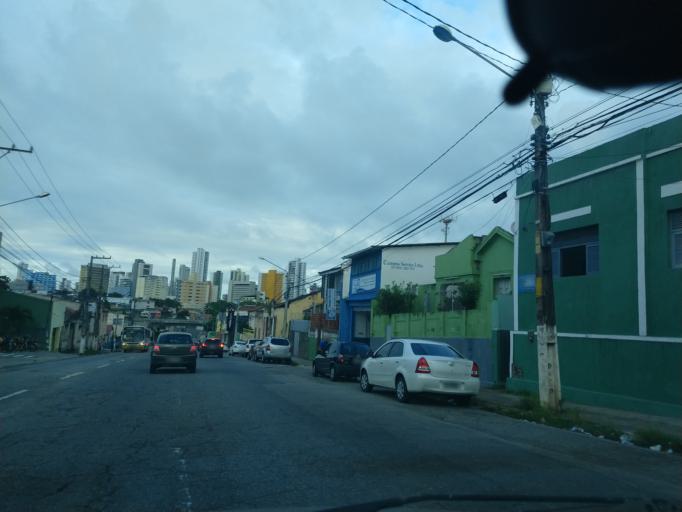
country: BR
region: Rio Grande do Norte
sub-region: Natal
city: Natal
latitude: -5.7921
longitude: -35.2113
